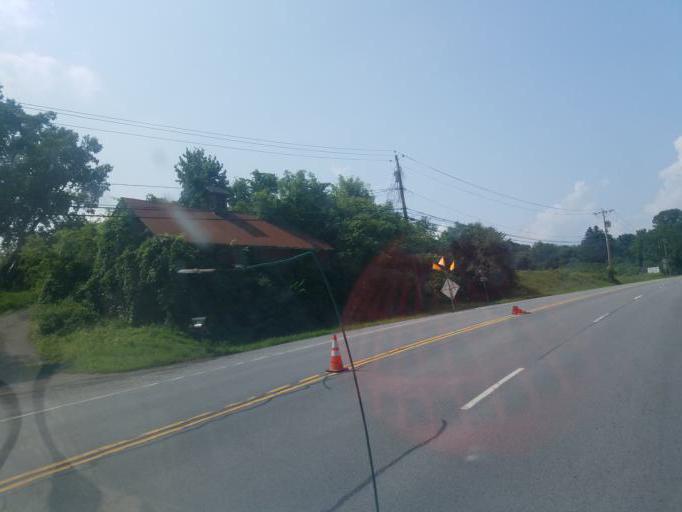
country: US
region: New York
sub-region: Montgomery County
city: Fonda
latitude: 42.9593
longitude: -74.3857
